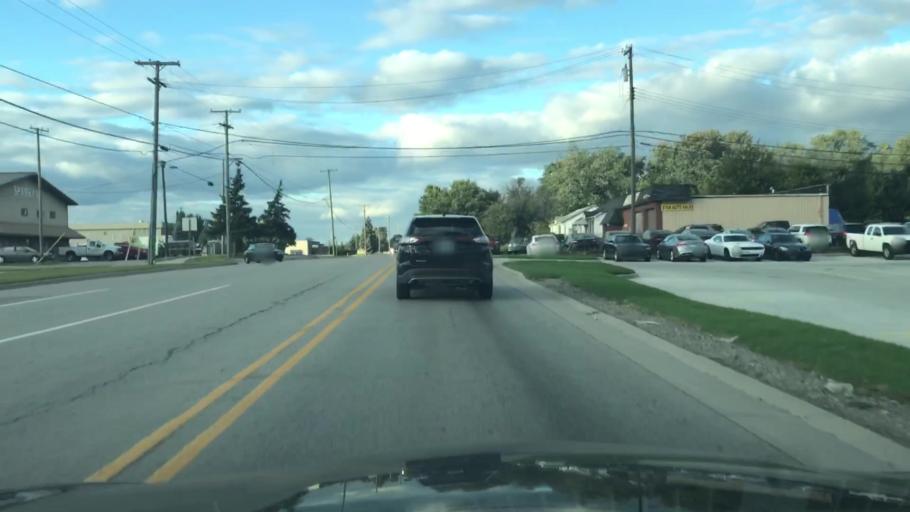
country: US
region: Michigan
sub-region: Macomb County
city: Utica
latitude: 42.6397
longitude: -83.0726
